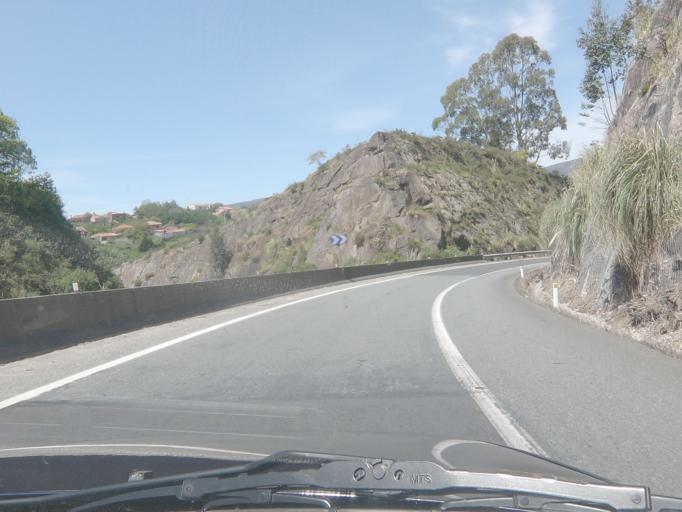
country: ES
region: Galicia
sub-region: Provincia de Pontevedra
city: Poio
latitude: 42.4152
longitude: -8.6513
